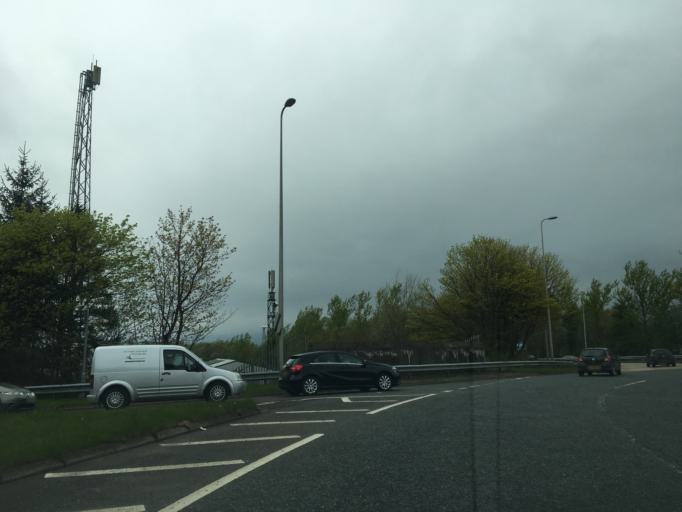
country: GB
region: Scotland
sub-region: Argyll and Bute
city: Cardross
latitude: 55.9297
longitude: -4.6448
